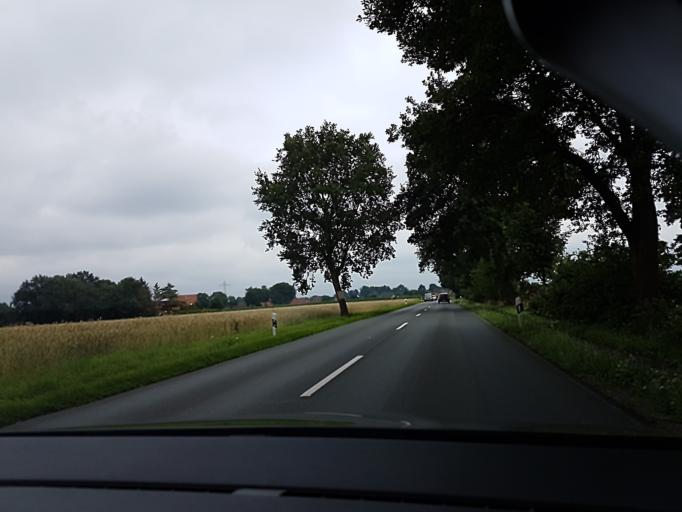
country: DE
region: Lower Saxony
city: Delmenhorst
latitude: 53.0331
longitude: 8.6832
